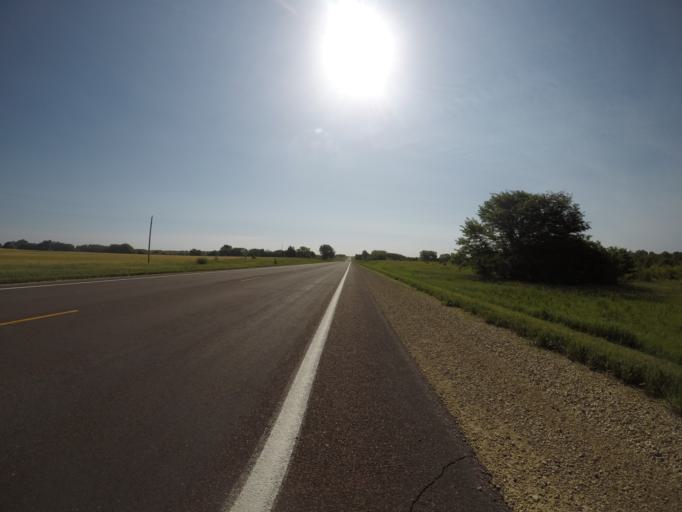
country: US
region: Kansas
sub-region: Riley County
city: Fort Riley North
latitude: 39.3064
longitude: -96.8938
